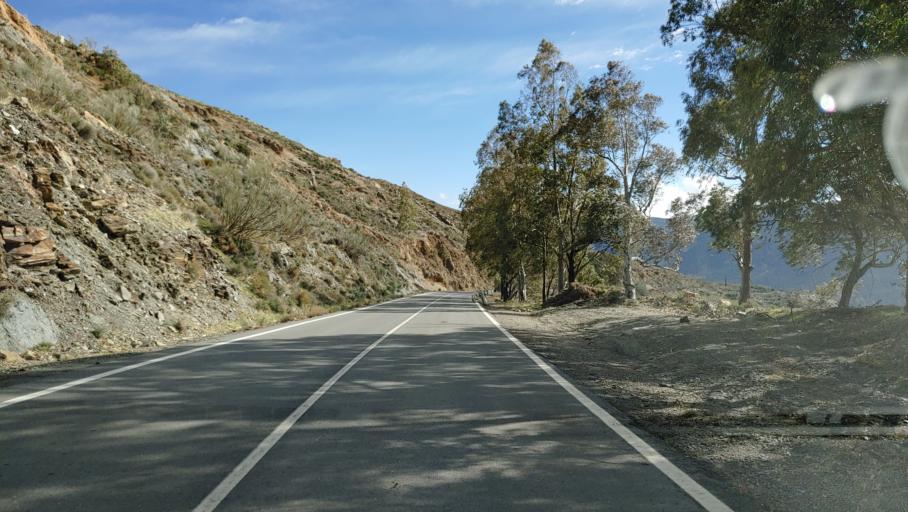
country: ES
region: Andalusia
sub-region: Provincia de Almeria
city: Ohanes
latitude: 37.0325
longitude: -2.7406
